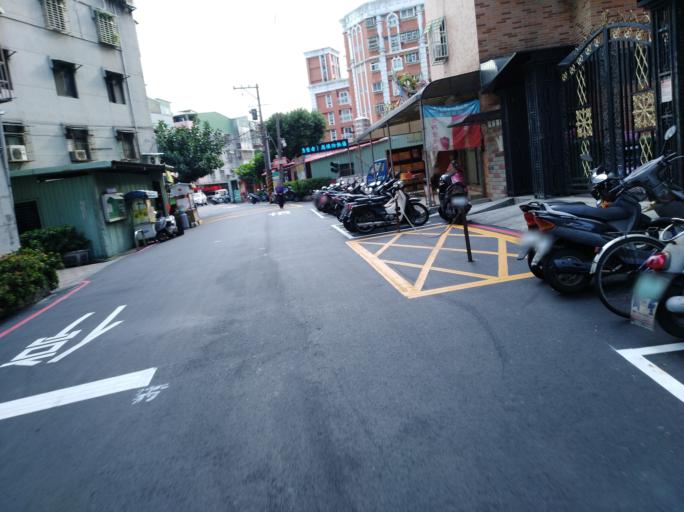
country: TW
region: Taipei
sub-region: Taipei
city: Banqiao
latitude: 25.0418
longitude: 121.4258
